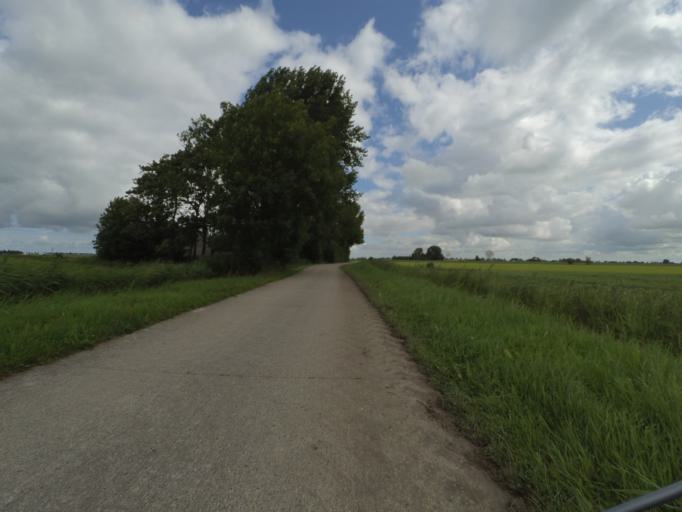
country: NL
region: Friesland
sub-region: Gemeente Kollumerland en Nieuwkruisland
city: Kollum
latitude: 53.2762
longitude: 6.1990
